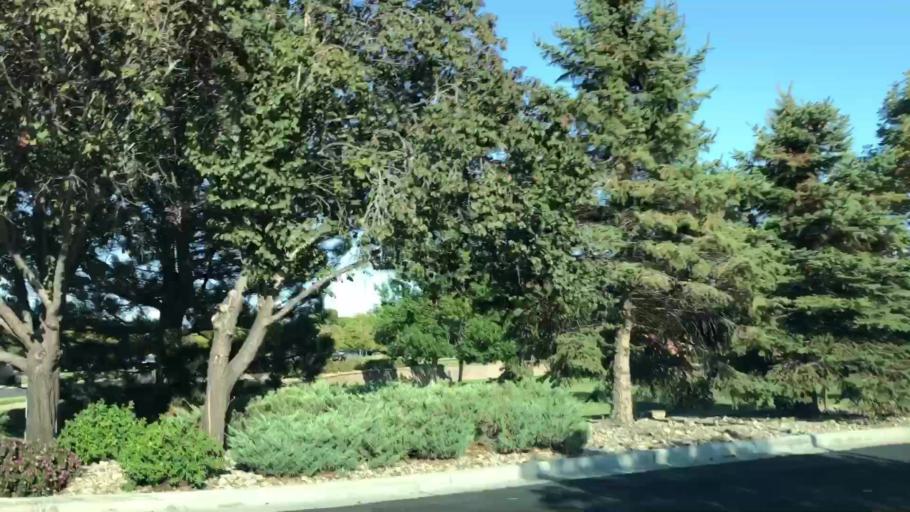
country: US
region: Colorado
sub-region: Larimer County
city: Loveland
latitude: 40.4080
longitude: -105.0052
